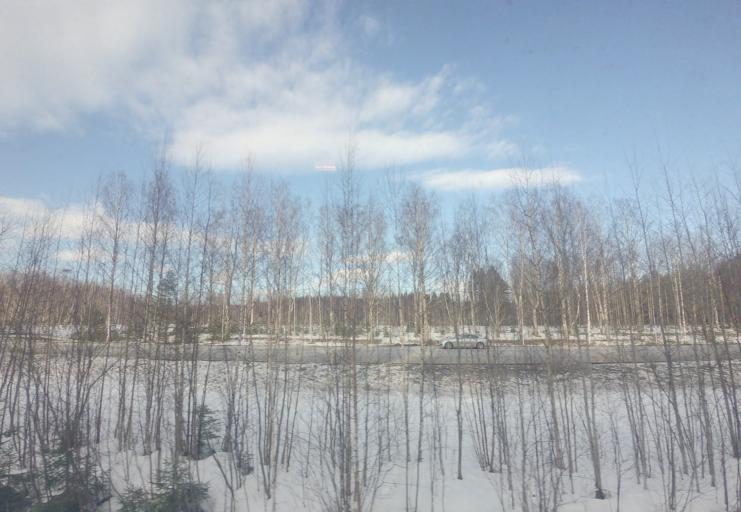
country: FI
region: Southern Savonia
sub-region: Savonlinna
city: Punkaharju
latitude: 61.7982
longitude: 29.3273
